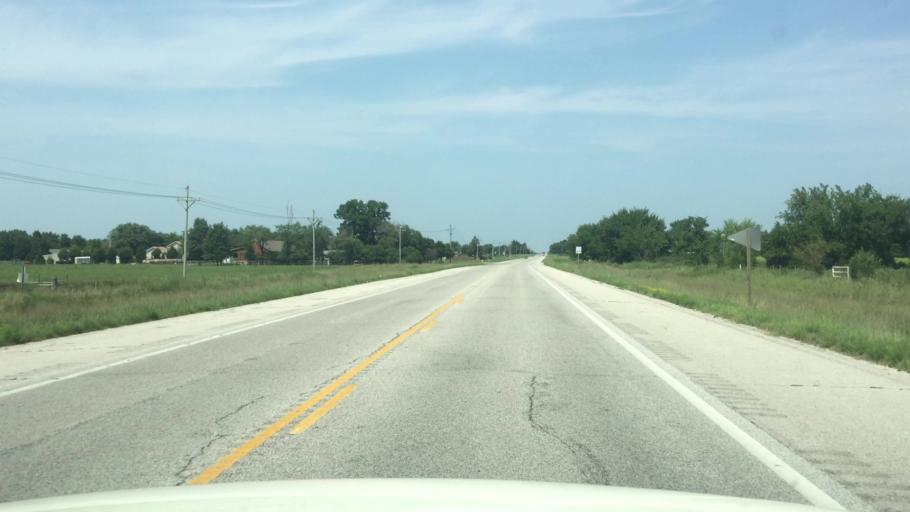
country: US
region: Kansas
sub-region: Cherokee County
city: Galena
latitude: 37.0909
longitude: -94.7044
